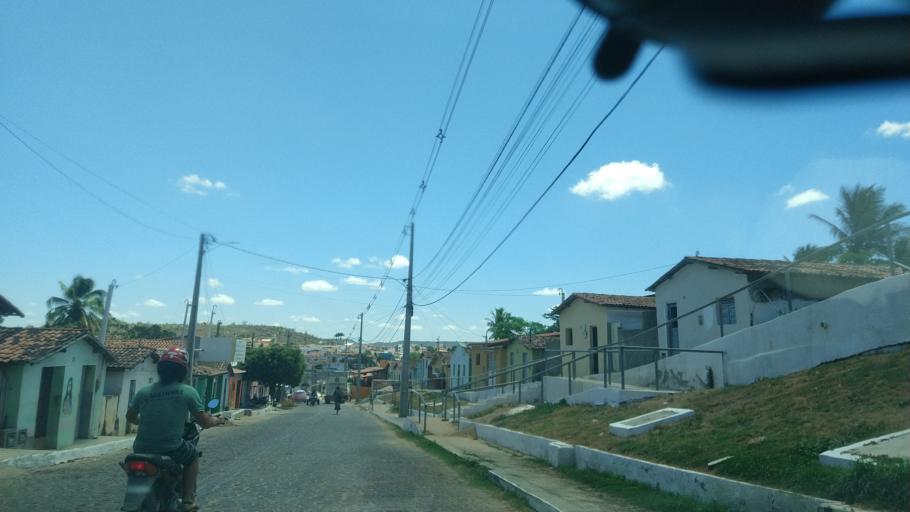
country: BR
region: Rio Grande do Norte
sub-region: Cerro Cora
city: Cerro Cora
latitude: -6.0372
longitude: -36.3471
